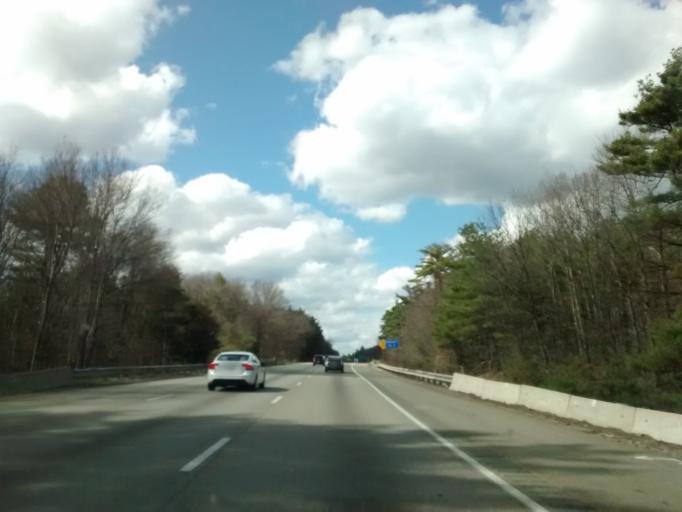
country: US
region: Massachusetts
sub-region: Middlesex County
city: Hopkinton
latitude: 42.2289
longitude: -71.5498
